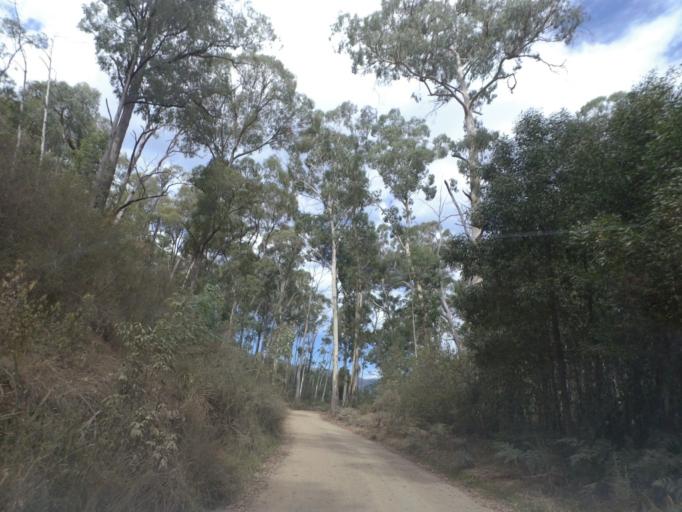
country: AU
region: Victoria
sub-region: Murrindindi
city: Alexandra
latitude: -37.3687
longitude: 145.7559
